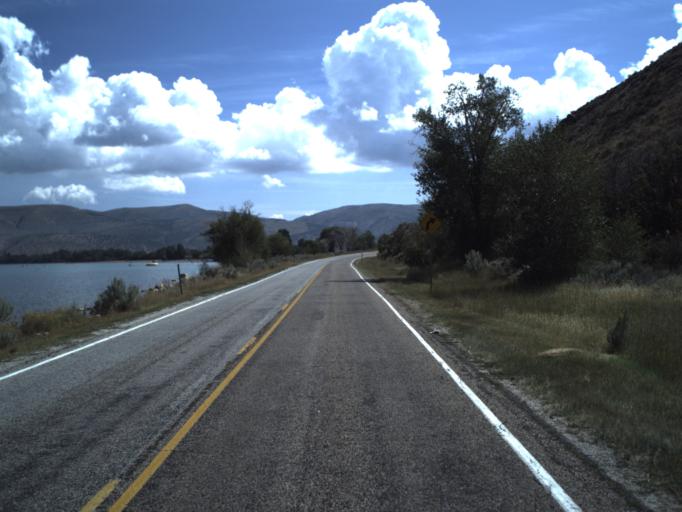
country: US
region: Utah
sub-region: Rich County
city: Randolph
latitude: 41.8500
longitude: -111.3566
